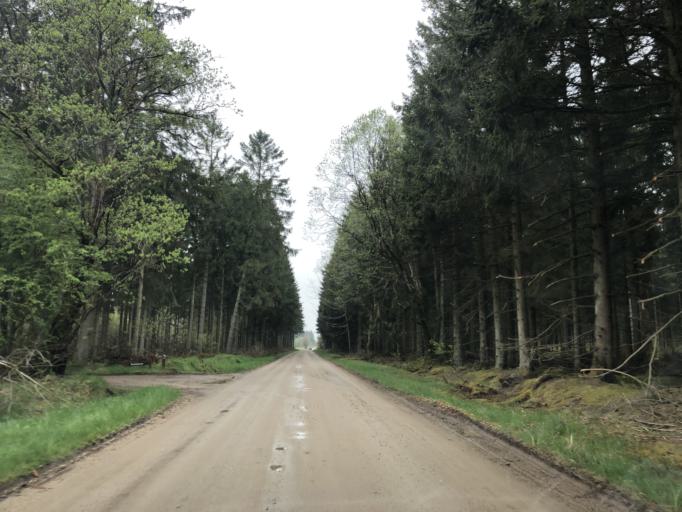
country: DK
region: Central Jutland
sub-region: Lemvig Kommune
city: Lemvig
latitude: 56.5004
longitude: 8.3333
